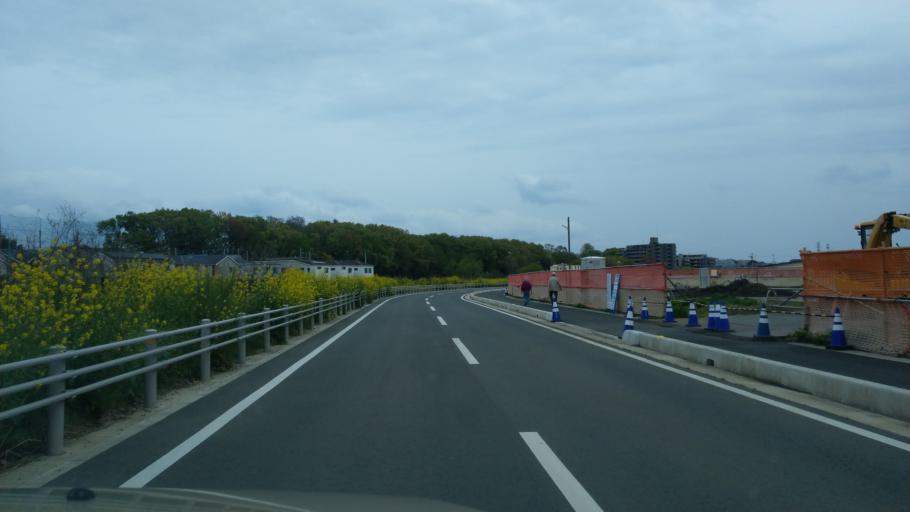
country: JP
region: Saitama
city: Ageoshimo
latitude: 35.9449
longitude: 139.5985
